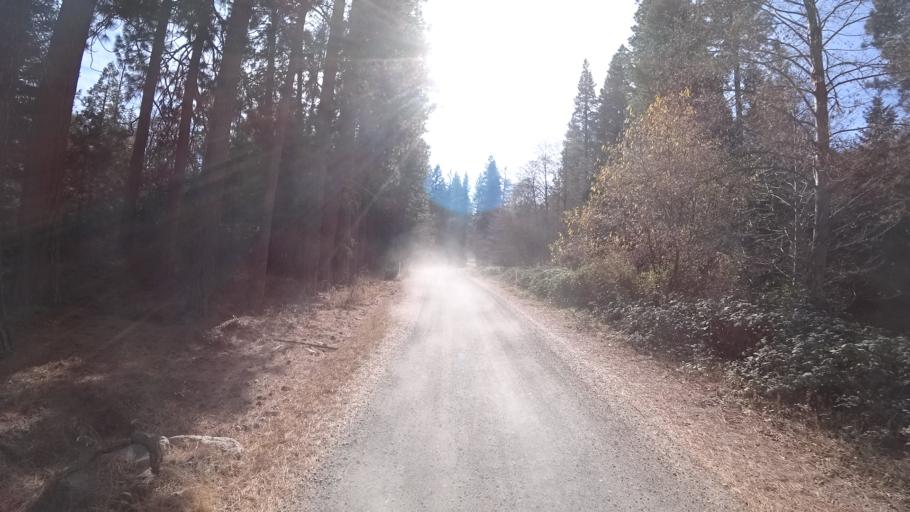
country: US
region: California
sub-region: Siskiyou County
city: Weed
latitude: 41.4378
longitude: -122.4240
